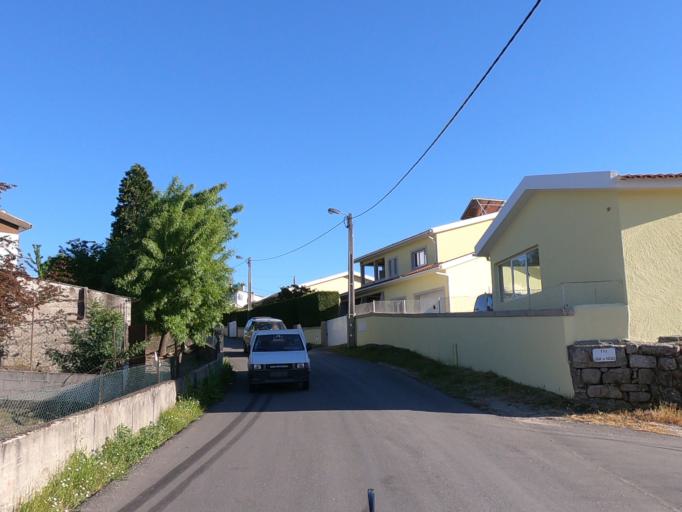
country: PT
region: Vila Real
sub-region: Vila Real
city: Vila Real
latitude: 41.3231
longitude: -7.6945
